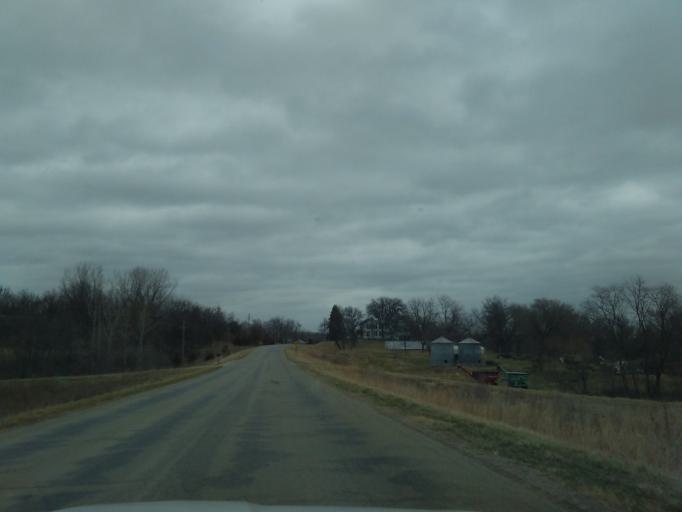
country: US
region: Nebraska
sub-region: Richardson County
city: Falls City
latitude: 40.0422
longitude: -95.4261
